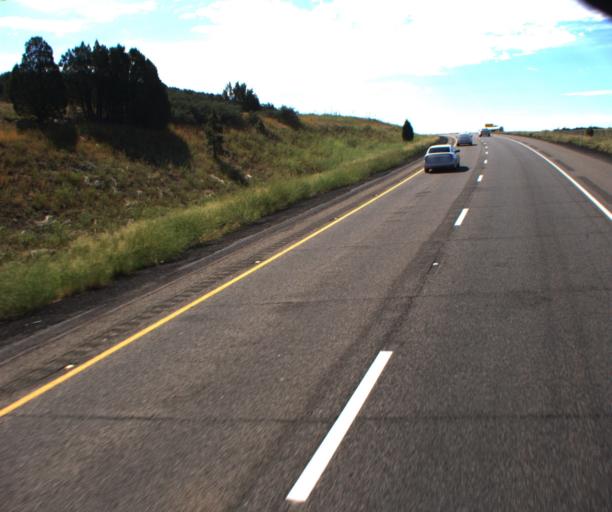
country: US
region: Arizona
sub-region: Yavapai County
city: Village of Oak Creek (Big Park)
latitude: 34.8142
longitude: -111.6119
